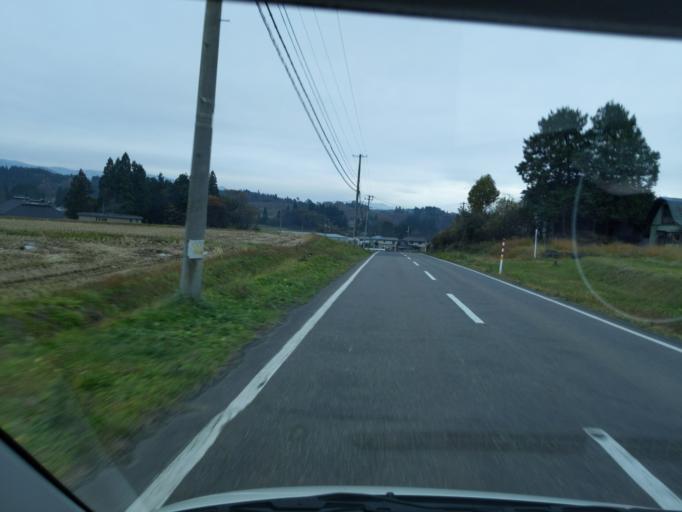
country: JP
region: Iwate
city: Kitakami
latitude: 39.2282
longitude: 141.2357
